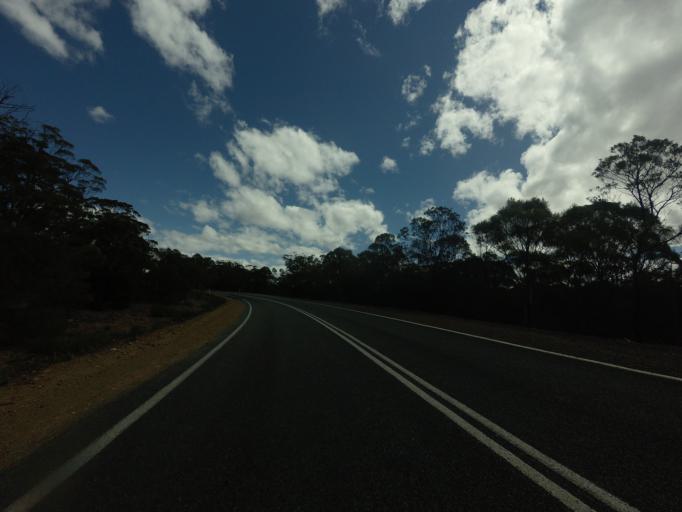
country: AU
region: Tasmania
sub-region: Break O'Day
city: St Helens
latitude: -42.0130
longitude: 147.9895
